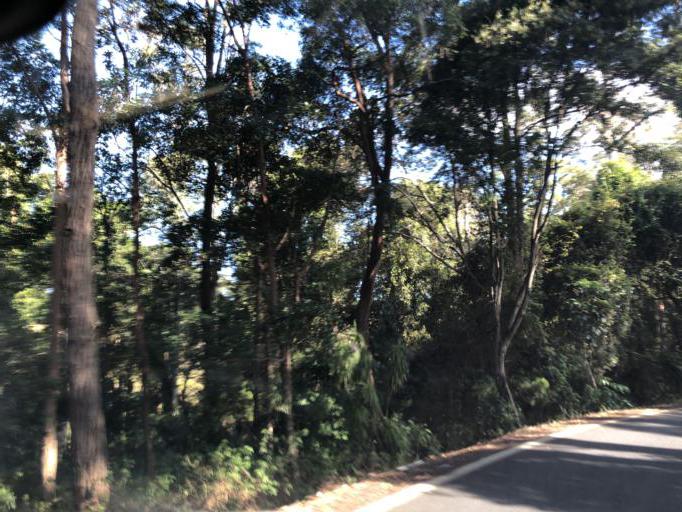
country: AU
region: New South Wales
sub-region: Coffs Harbour
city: Coffs Harbour
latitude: -30.2627
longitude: 153.1311
